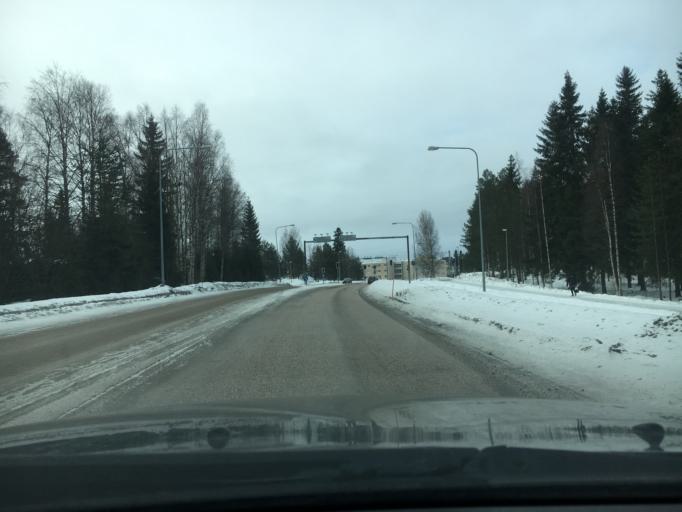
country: FI
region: Kainuu
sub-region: Kajaani
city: Kajaani
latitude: 64.2289
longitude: 27.7438
